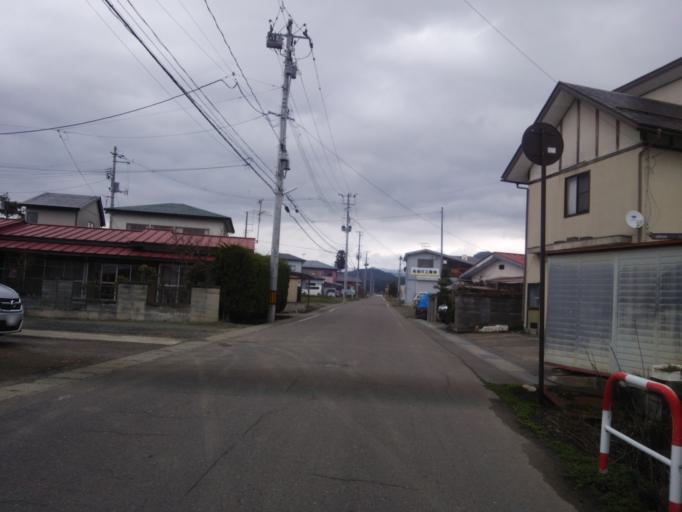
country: JP
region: Fukushima
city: Kitakata
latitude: 37.6580
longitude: 139.9031
